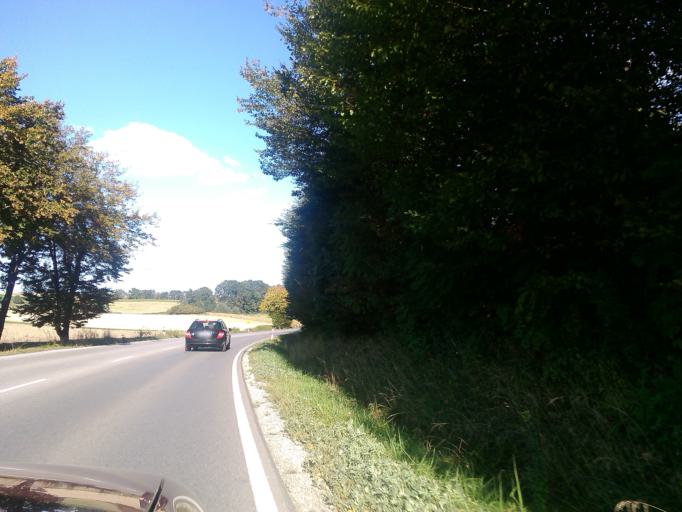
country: DE
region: Bavaria
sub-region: Swabia
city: Friedberg
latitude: 48.3680
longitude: 10.9965
